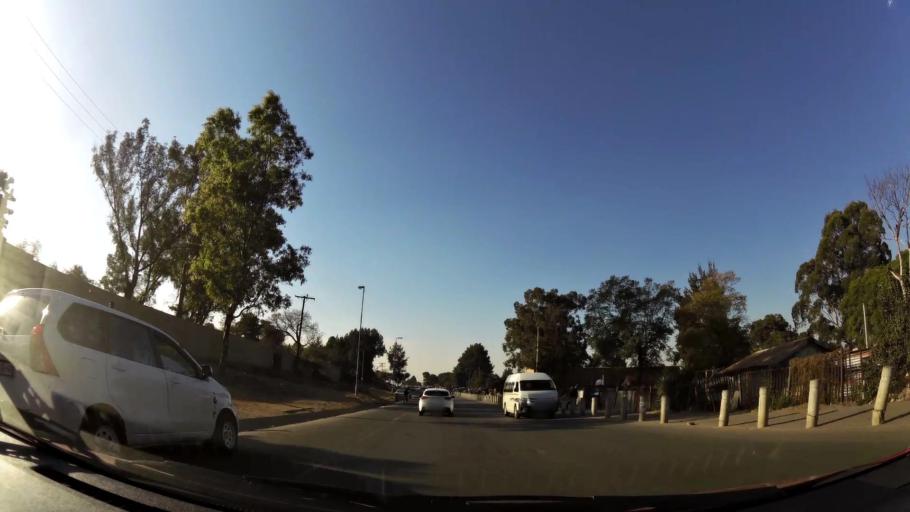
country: ZA
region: Gauteng
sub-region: West Rand District Municipality
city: Muldersdriseloop
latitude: -26.0563
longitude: 27.9037
